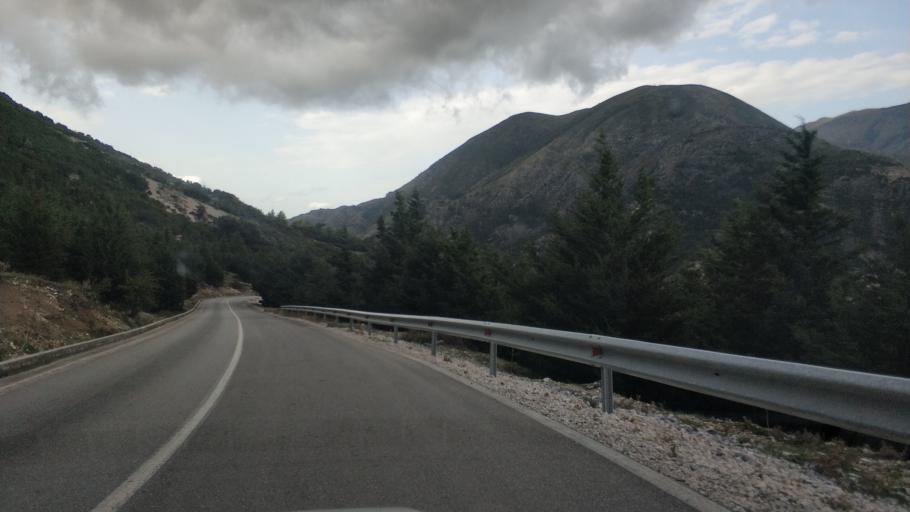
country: AL
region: Vlore
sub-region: Rrethi i Vlores
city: Orikum
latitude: 40.2395
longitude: 19.5515
